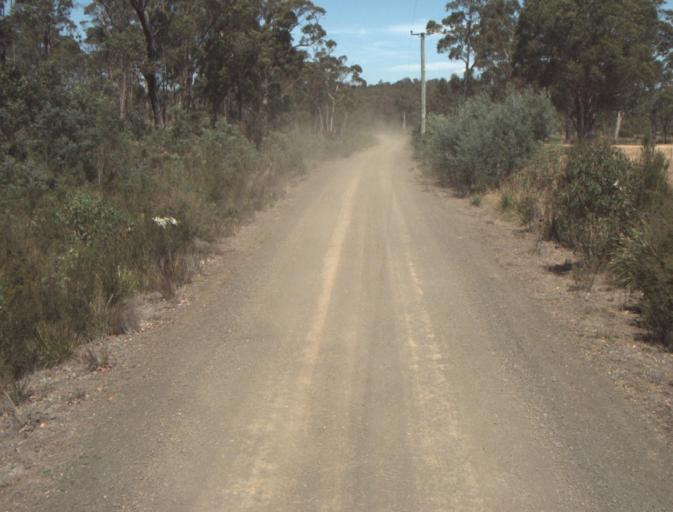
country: AU
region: Tasmania
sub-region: Launceston
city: Mayfield
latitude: -41.2733
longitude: 147.0993
